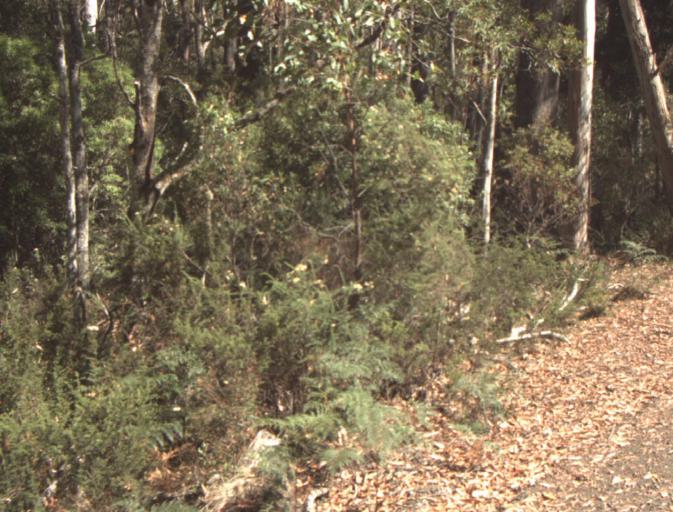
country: AU
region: Tasmania
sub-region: Launceston
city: Newstead
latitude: -41.3060
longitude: 147.3344
